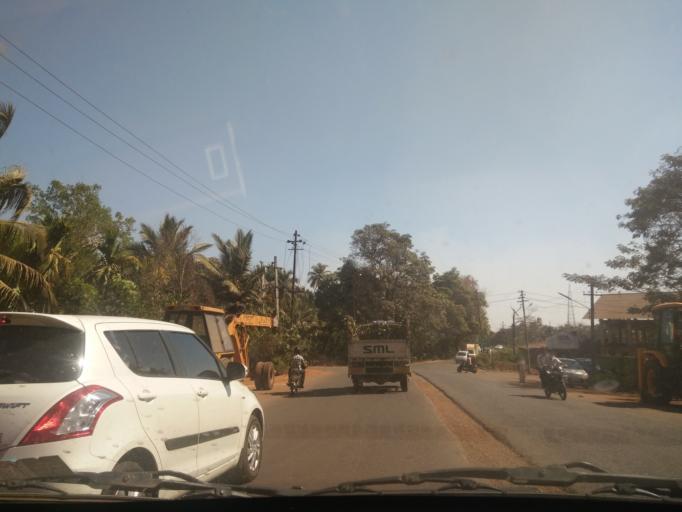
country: IN
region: Goa
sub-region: North Goa
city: Dicholi
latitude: 15.5895
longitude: 73.9494
